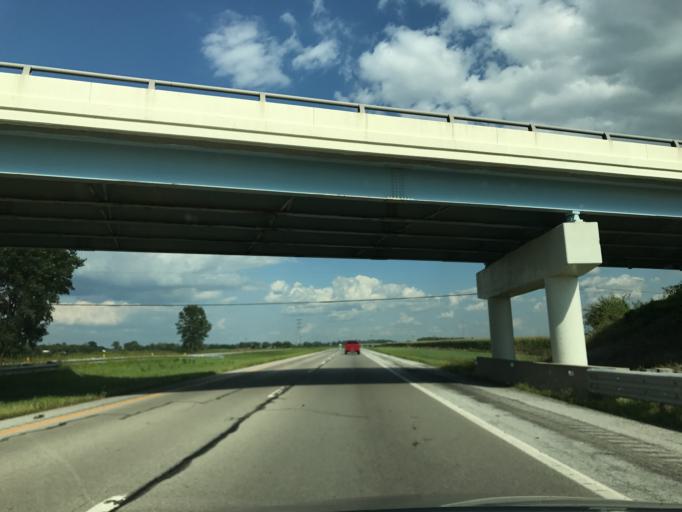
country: US
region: Ohio
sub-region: Allen County
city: Elida
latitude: 40.8350
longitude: -84.1841
